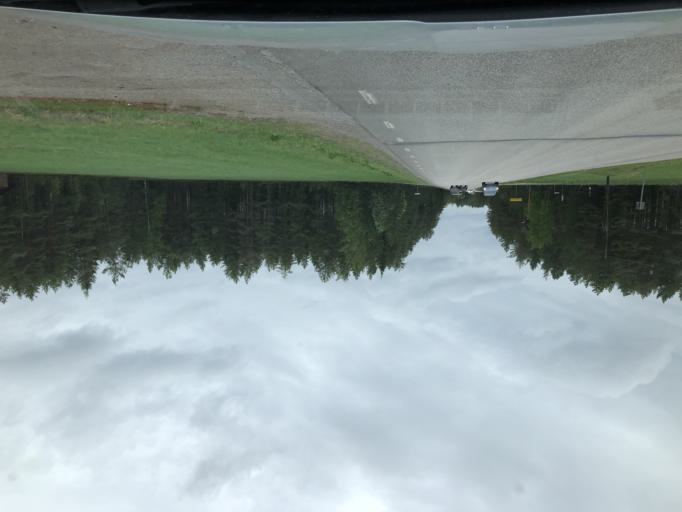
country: SE
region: Norrbotten
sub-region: Pitea Kommun
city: Bergsviken
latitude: 65.3711
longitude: 21.3554
